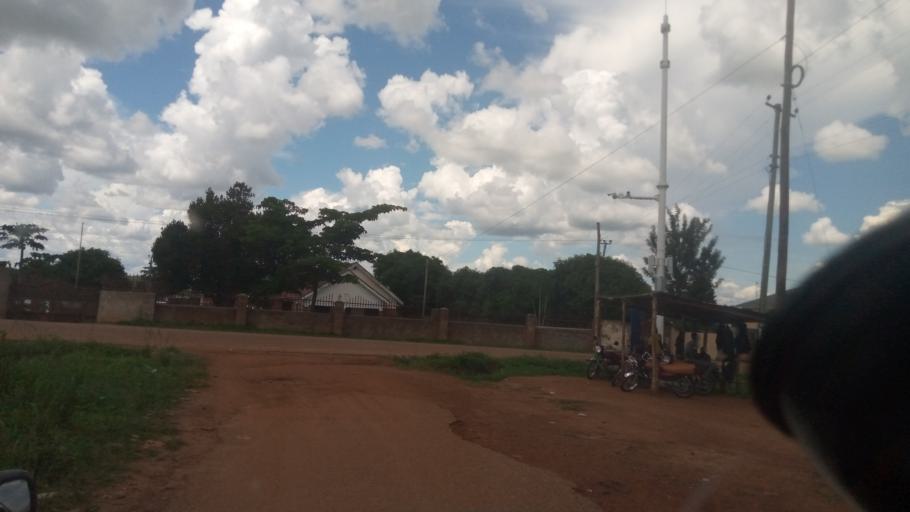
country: UG
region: Northern Region
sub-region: Lira District
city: Lira
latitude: 2.2404
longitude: 32.9086
